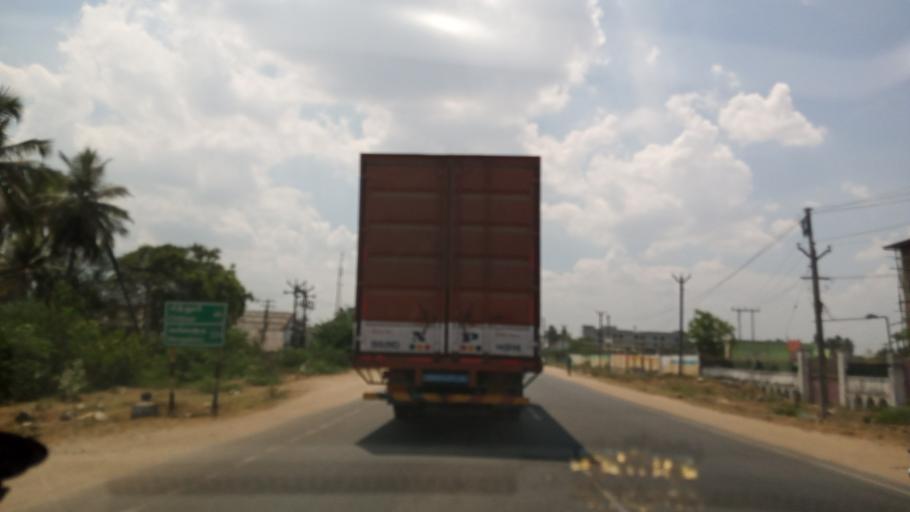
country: IN
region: Tamil Nadu
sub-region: Vellore
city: Walajapet
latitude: 12.9292
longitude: 79.3410
